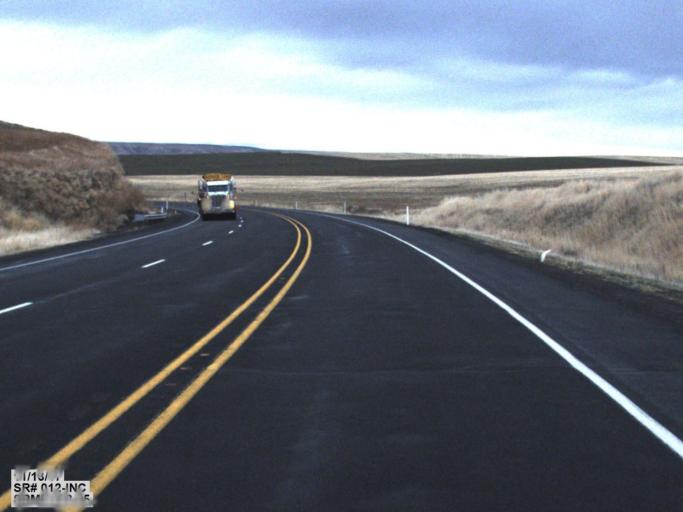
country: US
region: Washington
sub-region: Columbia County
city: Dayton
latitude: 46.3983
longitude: -117.9321
